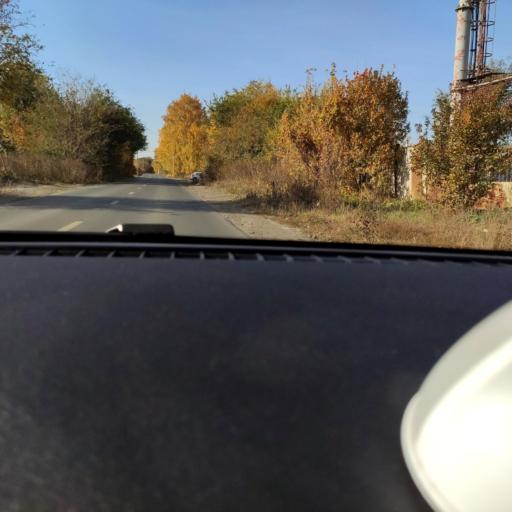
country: RU
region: Samara
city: Smyshlyayevka
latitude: 53.2439
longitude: 50.3592
